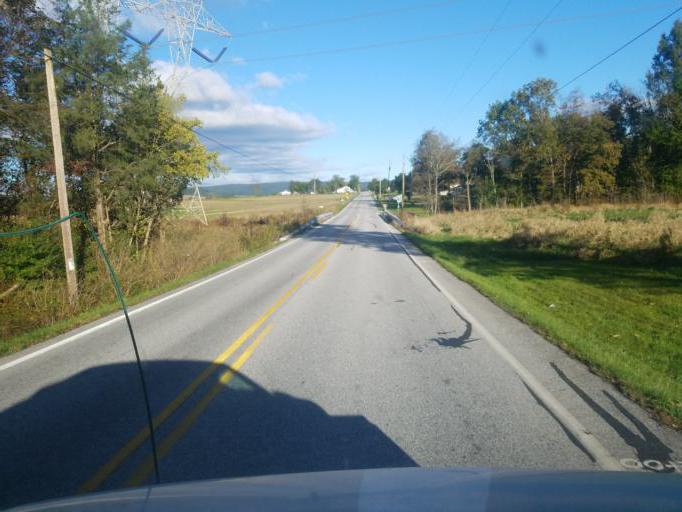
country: US
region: Pennsylvania
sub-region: Adams County
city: Biglerville
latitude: 39.8763
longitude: -77.2804
